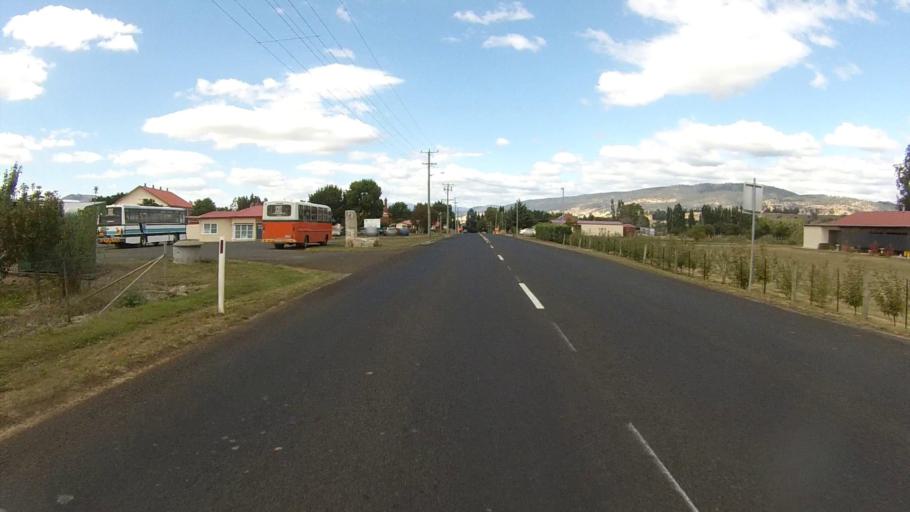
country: AU
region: Tasmania
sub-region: Derwent Valley
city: New Norfolk
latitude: -42.6958
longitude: 146.8882
